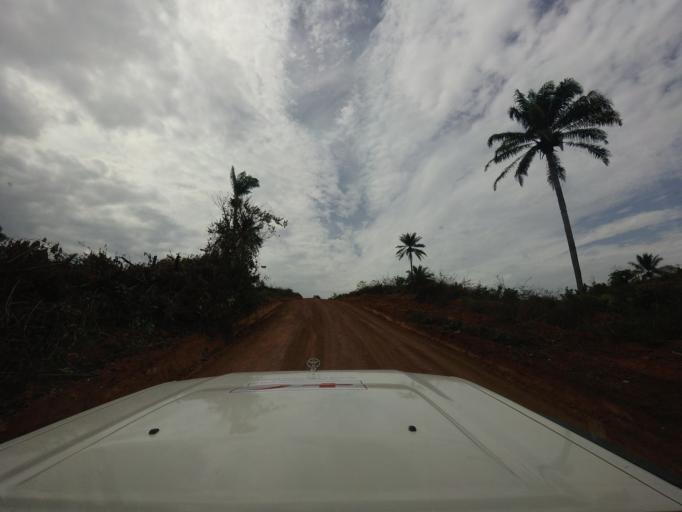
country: SL
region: Eastern Province
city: Buedu
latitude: 8.2181
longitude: -10.2223
